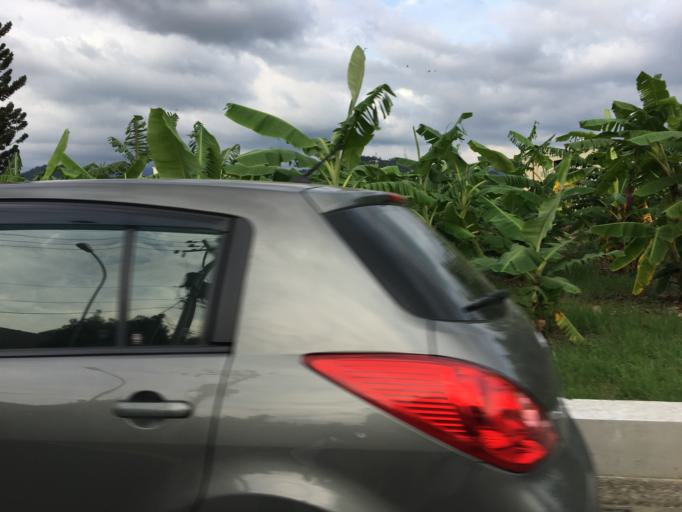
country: TW
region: Taiwan
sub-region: Taichung City
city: Taichung
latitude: 24.0902
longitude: 120.7104
